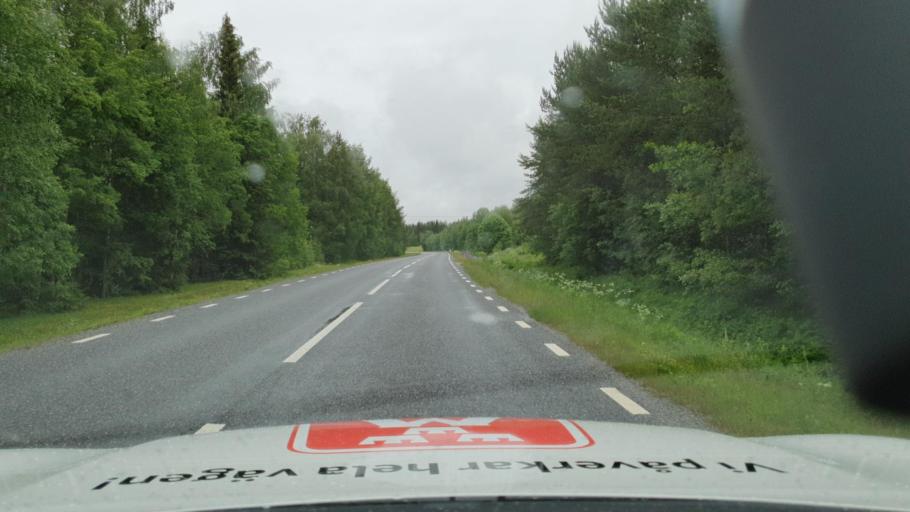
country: SE
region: Vaesterbotten
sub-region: Asele Kommun
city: Asele
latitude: 63.9733
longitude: 17.2632
